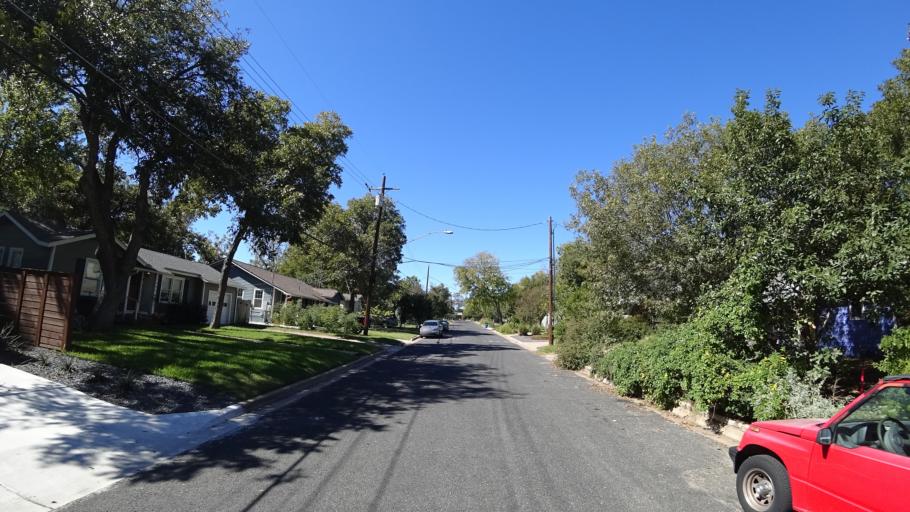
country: US
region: Texas
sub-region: Travis County
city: Austin
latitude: 30.3343
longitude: -97.7368
